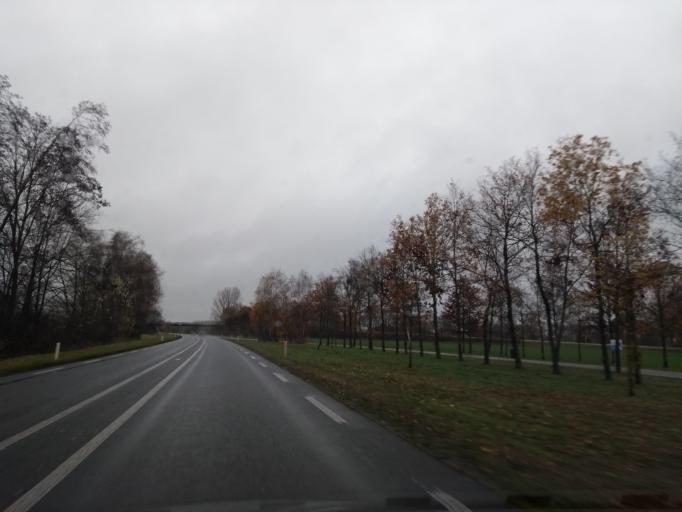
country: NL
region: Overijssel
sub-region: Gemeente Wierden
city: Wierden
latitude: 52.3097
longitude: 6.5509
